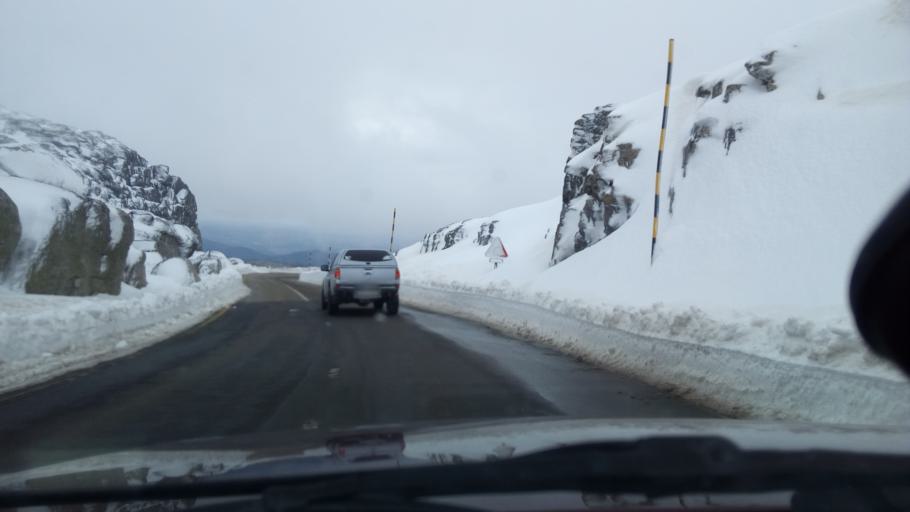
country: PT
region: Guarda
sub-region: Manteigas
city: Manteigas
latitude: 40.3263
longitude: -7.6015
